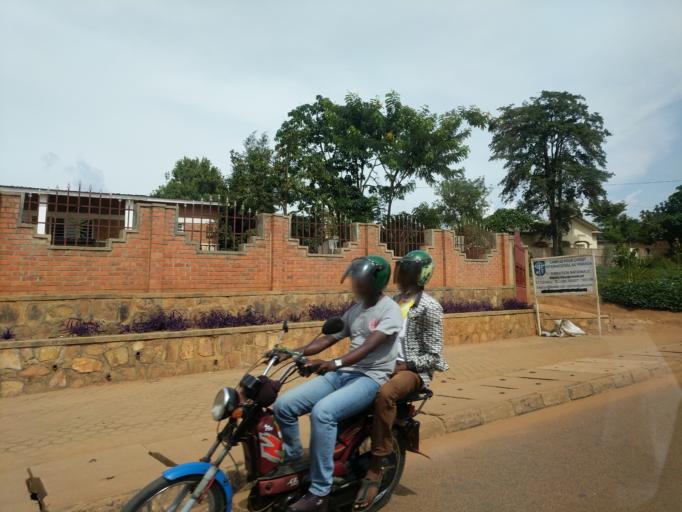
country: RW
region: Kigali
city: Kigali
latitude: -1.9729
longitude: 30.1344
